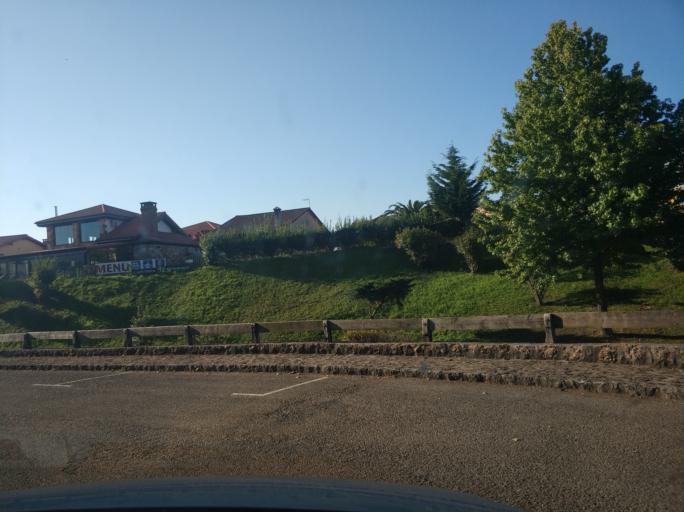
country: ES
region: Cantabria
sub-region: Provincia de Cantabria
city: Penagos
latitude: 43.3590
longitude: -3.8230
